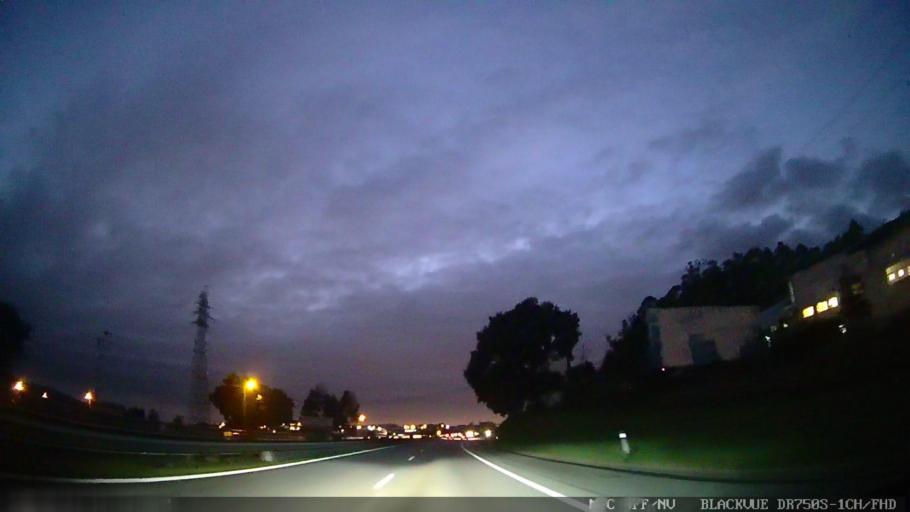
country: PT
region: Porto
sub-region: Lousada
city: Meinedo
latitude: 41.2191
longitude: -8.2505
